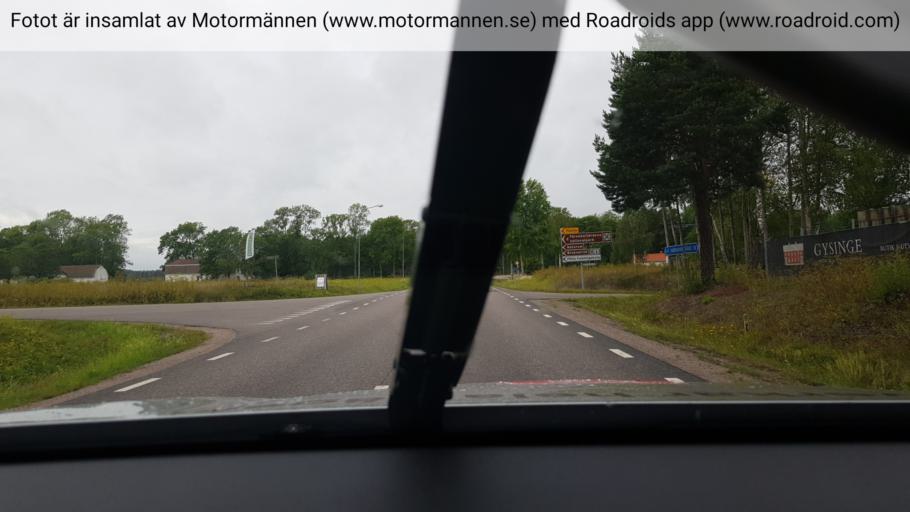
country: SE
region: Uppsala
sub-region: Heby Kommun
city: Tarnsjo
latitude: 60.2912
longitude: 16.8861
